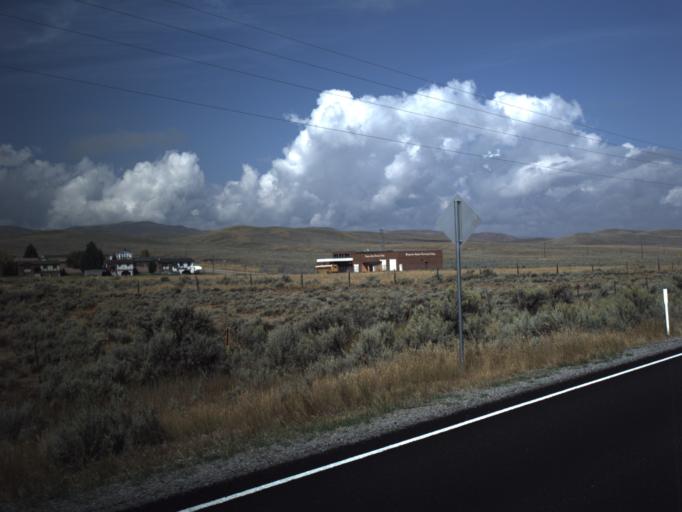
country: US
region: Utah
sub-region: Rich County
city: Randolph
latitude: 41.5856
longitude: -111.1684
